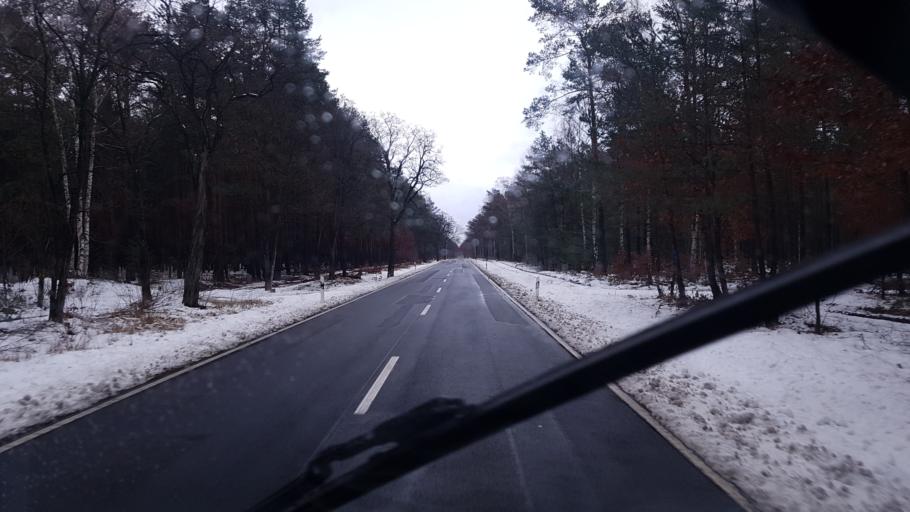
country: DE
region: Brandenburg
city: Tauer
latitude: 51.9794
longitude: 14.4918
